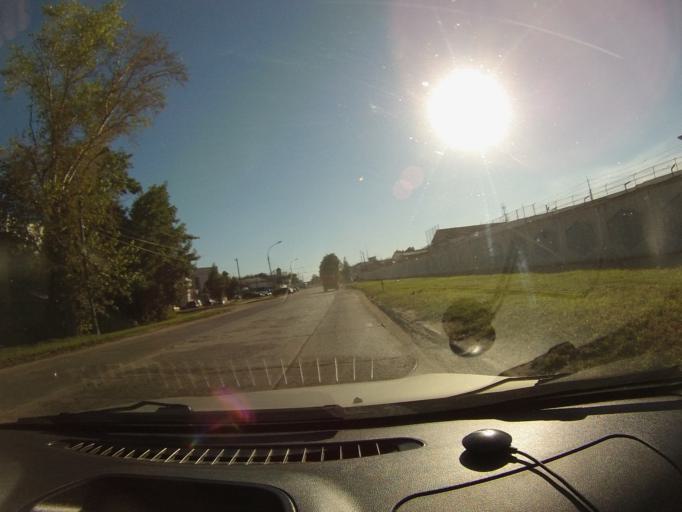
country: RU
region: Tambov
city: Tambov
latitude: 52.7392
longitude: 41.4427
